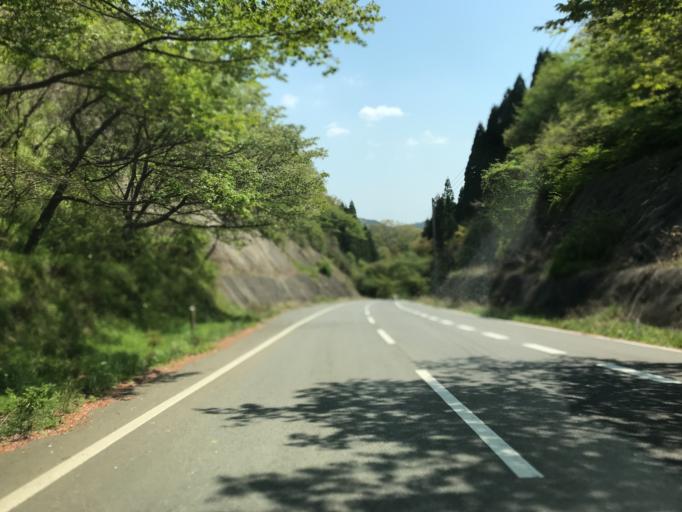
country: JP
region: Ibaraki
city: Kitaibaraki
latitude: 36.9584
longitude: 140.7006
